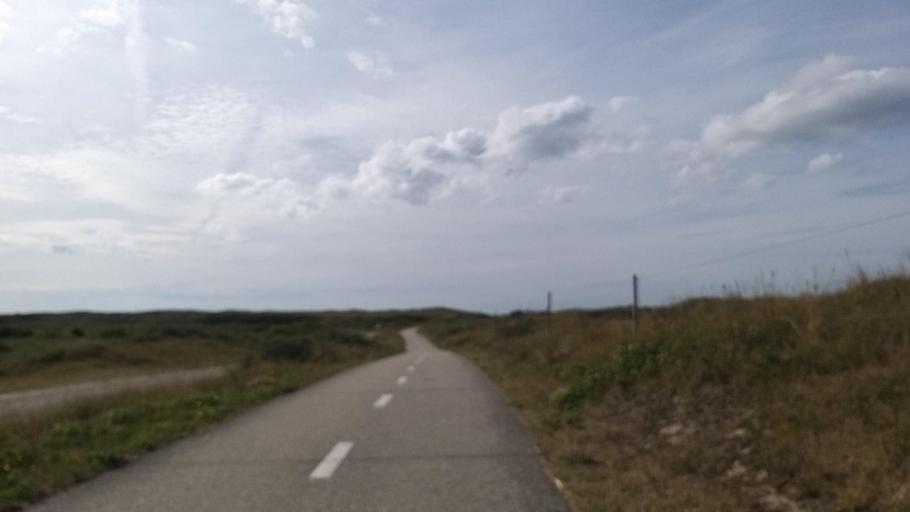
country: NL
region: North Holland
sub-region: Gemeente Texel
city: Den Burg
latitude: 53.1594
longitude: 4.8277
